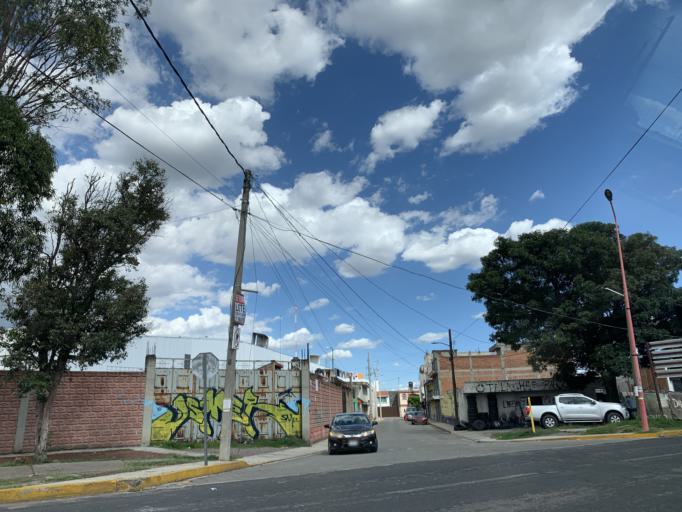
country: MX
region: Puebla
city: Cholula
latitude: 19.0710
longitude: -98.3156
